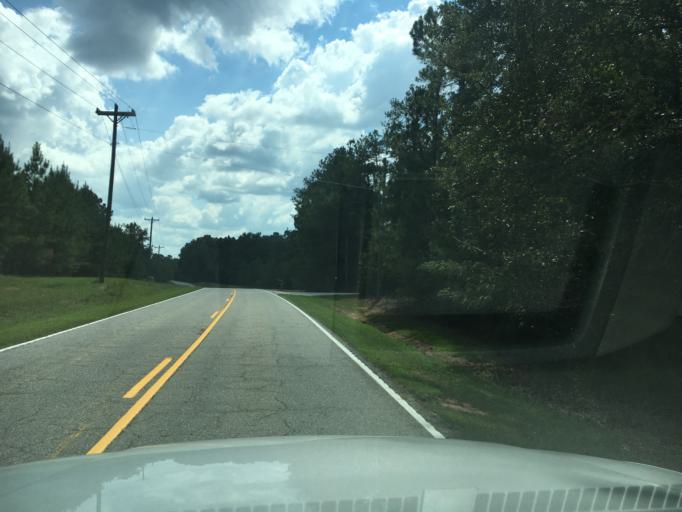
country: US
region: South Carolina
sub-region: Greenwood County
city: Greenwood
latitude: 34.1196
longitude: -82.1269
